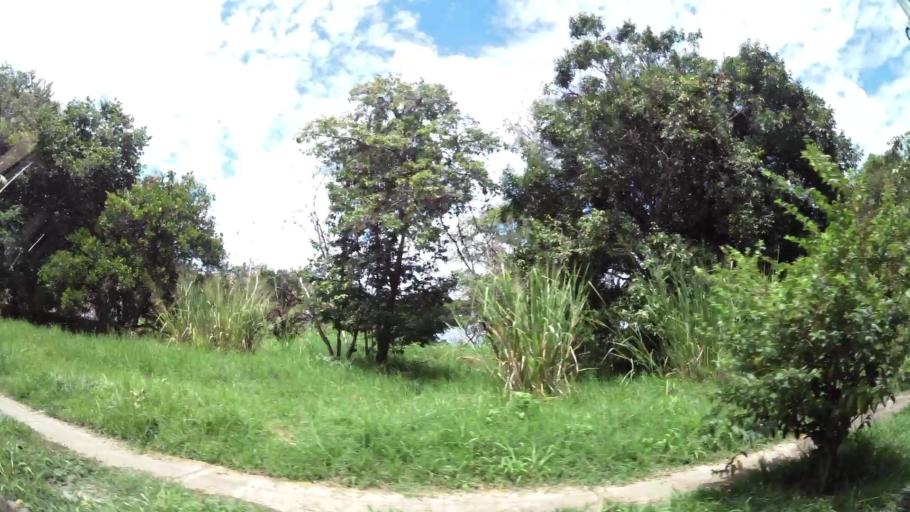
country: CO
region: Valle del Cauca
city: Cali
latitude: 3.3806
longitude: -76.5100
